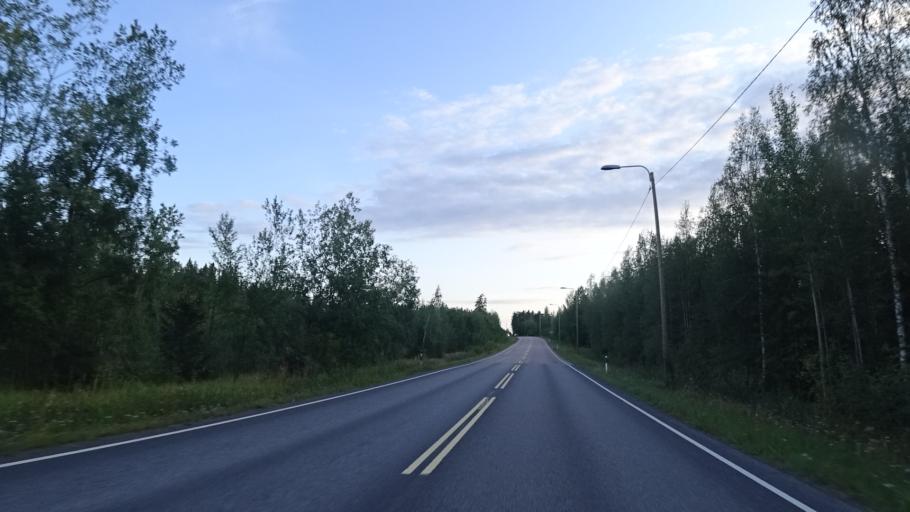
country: FI
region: Kymenlaakso
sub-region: Kotka-Hamina
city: Miehikkaelae
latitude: 60.6465
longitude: 27.8837
